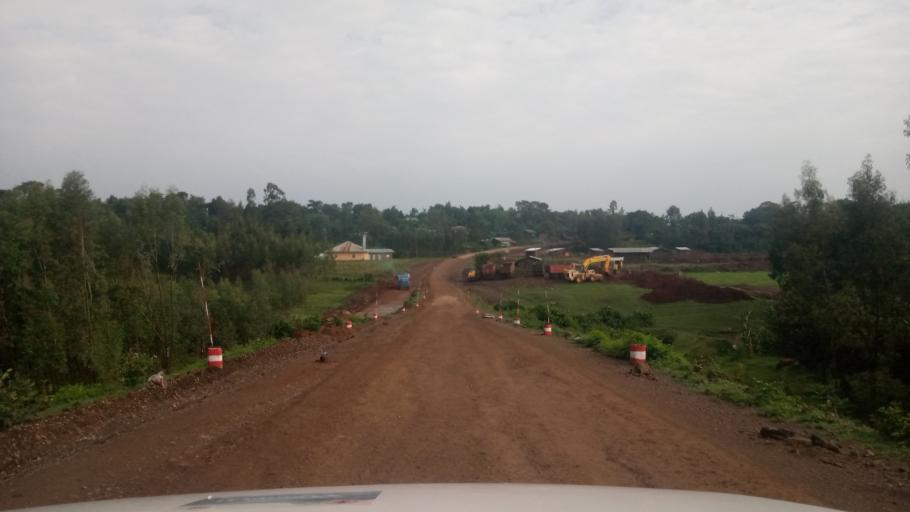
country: ET
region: Oromiya
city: Agaro
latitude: 7.8560
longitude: 36.6535
